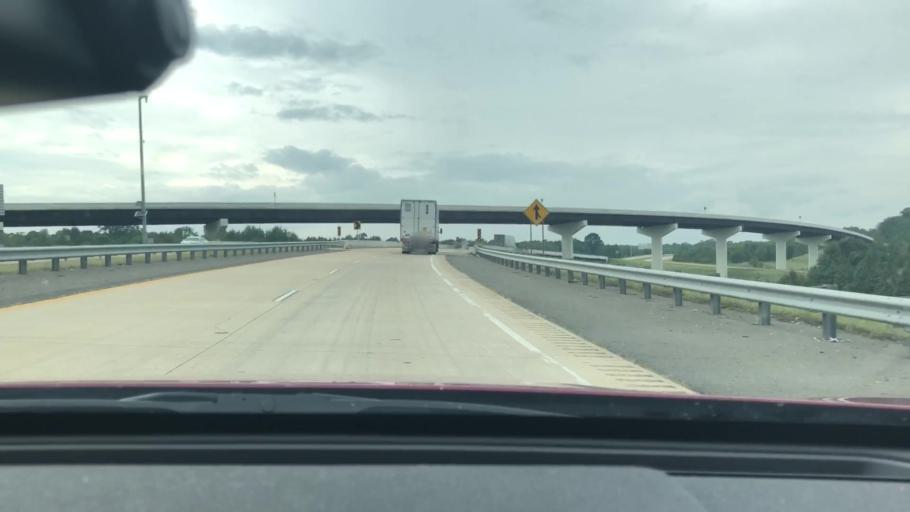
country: US
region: Texas
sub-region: Bowie County
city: Texarkana
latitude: 33.3882
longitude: -94.0186
